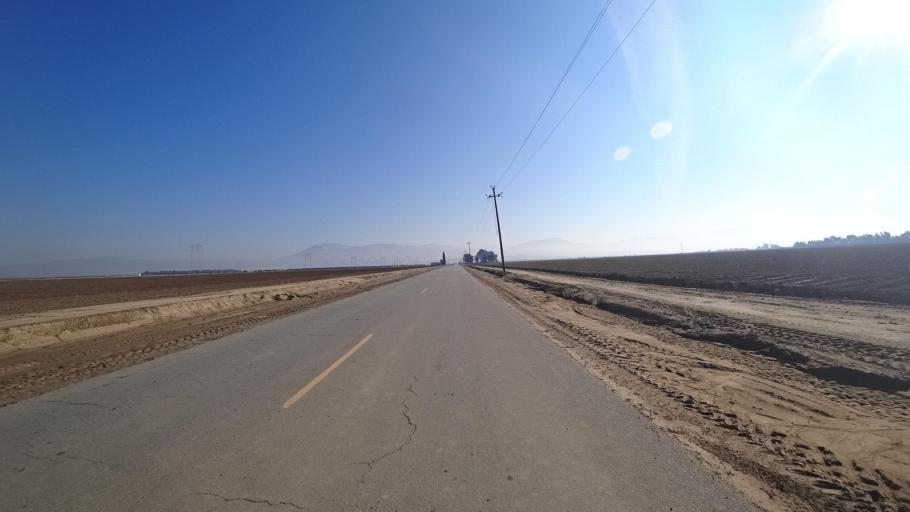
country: US
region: California
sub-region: Kern County
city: Weedpatch
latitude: 35.1219
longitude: -118.9318
